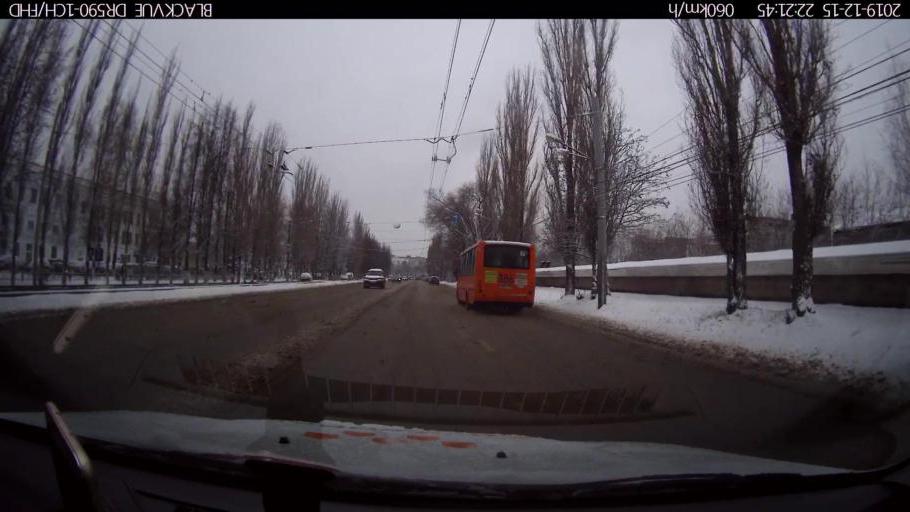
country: RU
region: Nizjnij Novgorod
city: Nizhniy Novgorod
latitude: 56.3341
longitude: 43.8922
